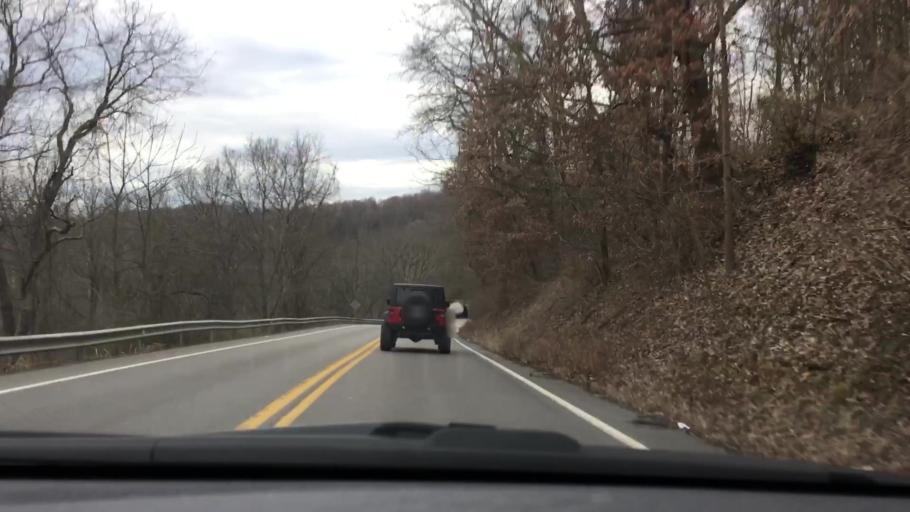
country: US
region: Pennsylvania
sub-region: Washington County
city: Cecil-Bishop
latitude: 40.3246
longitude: -80.2331
